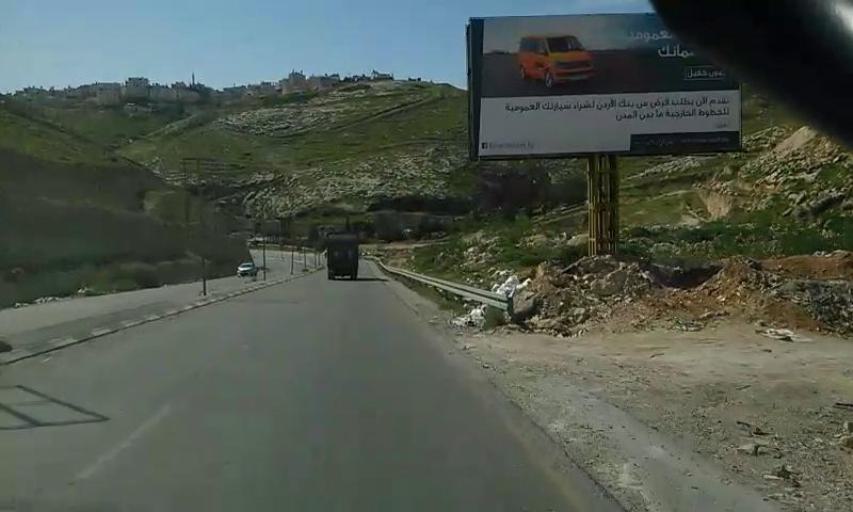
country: PS
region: West Bank
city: Abu Dis
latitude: 31.7467
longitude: 35.2808
